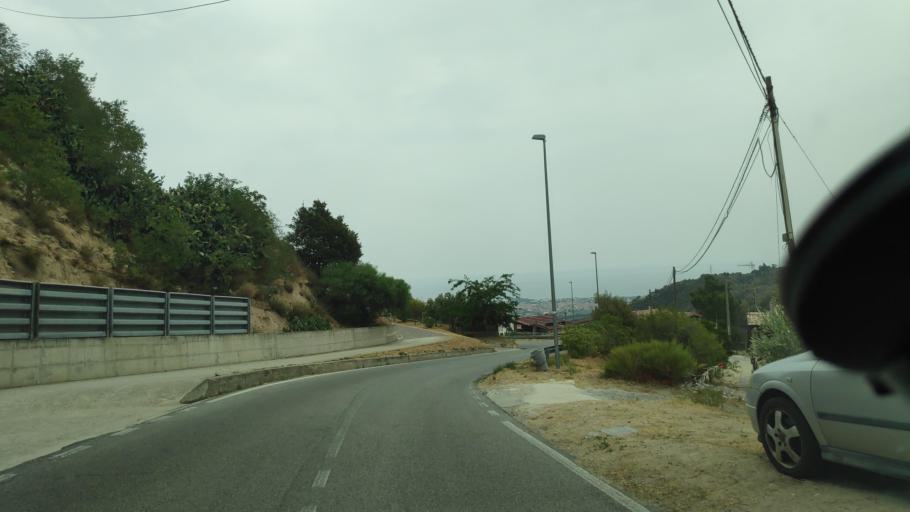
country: IT
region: Calabria
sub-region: Provincia di Catanzaro
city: Davoli
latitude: 38.6626
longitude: 16.5042
